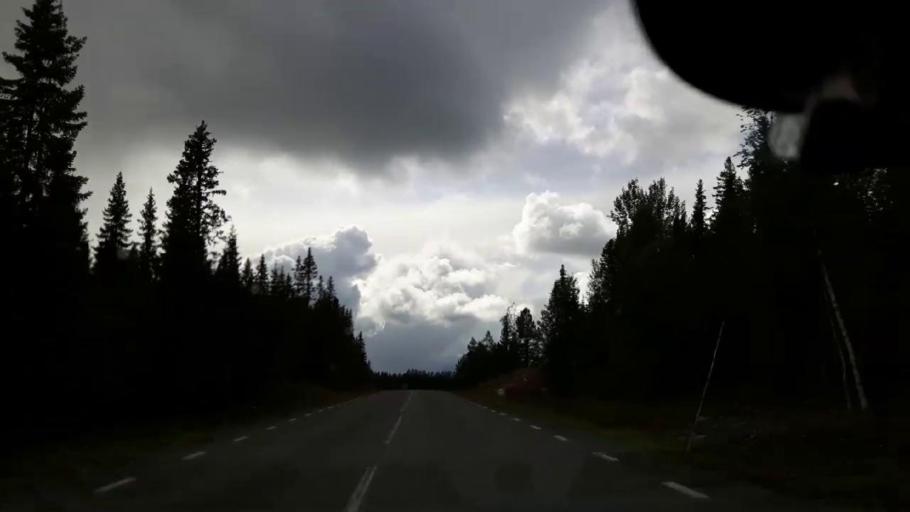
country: SE
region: Jaemtland
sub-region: Krokoms Kommun
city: Valla
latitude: 63.4357
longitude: 13.8174
